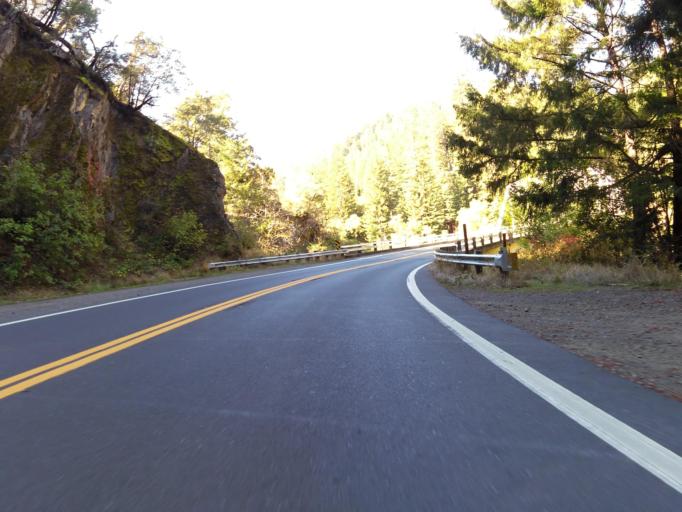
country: US
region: California
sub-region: Humboldt County
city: Redway
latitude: 39.8642
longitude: -123.7212
